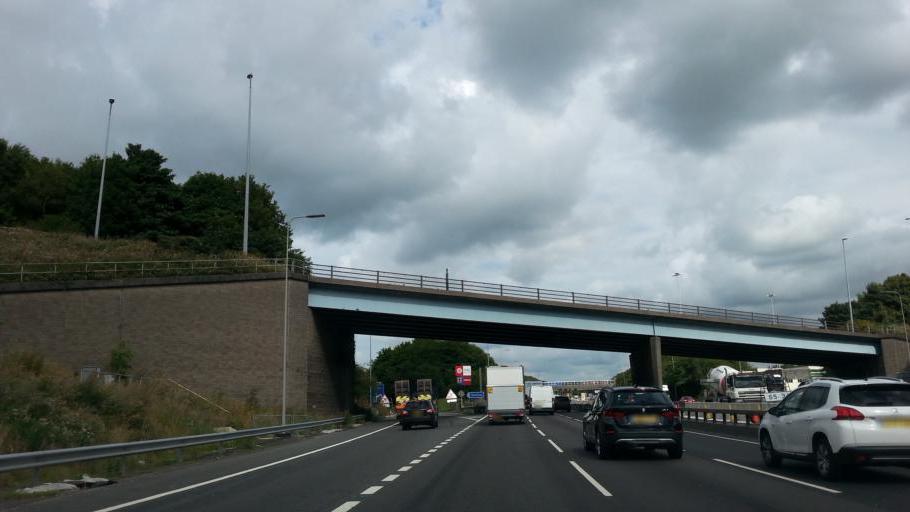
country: GB
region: England
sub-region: Manchester
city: Heywood
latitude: 53.5661
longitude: -2.2356
